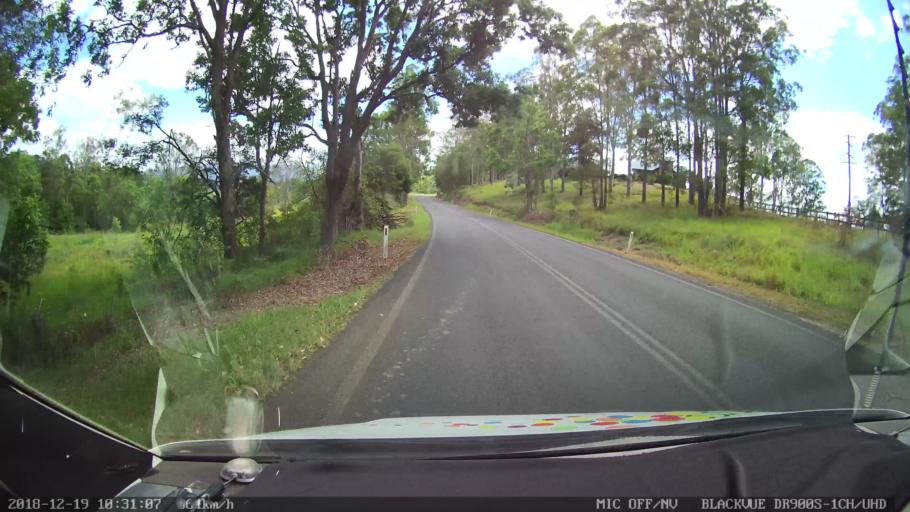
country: AU
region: New South Wales
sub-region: Lismore Municipality
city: Larnook
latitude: -28.5919
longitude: 153.1142
